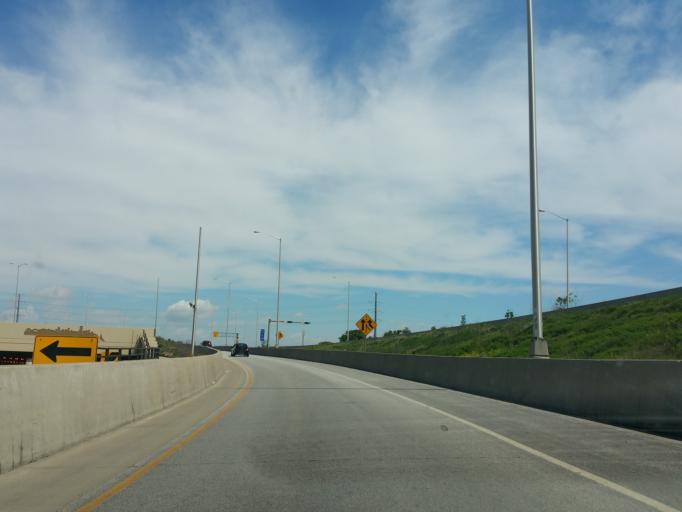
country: US
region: Wisconsin
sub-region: Milwaukee County
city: Saint Francis
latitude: 42.9591
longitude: -87.9336
